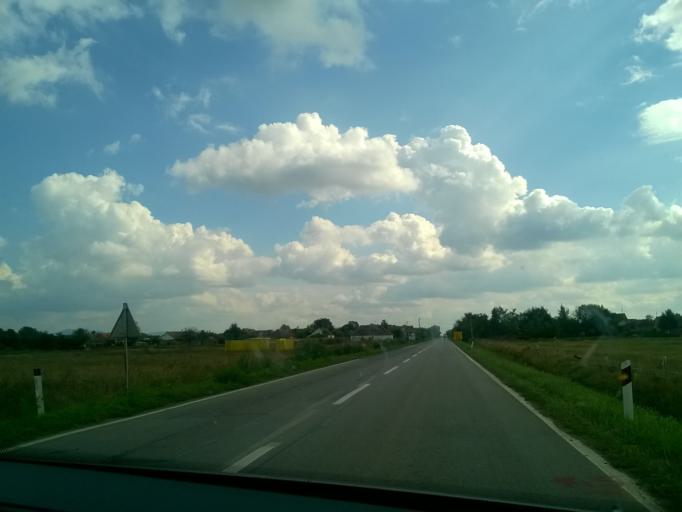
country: RS
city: Margita
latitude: 45.2194
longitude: 21.1733
